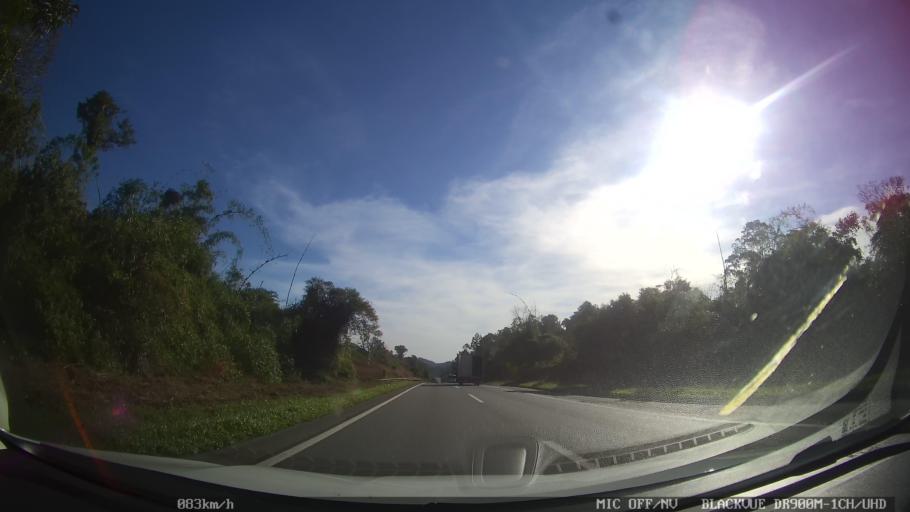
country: BR
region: Parana
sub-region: Antonina
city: Antonina
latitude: -25.1083
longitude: -48.7731
